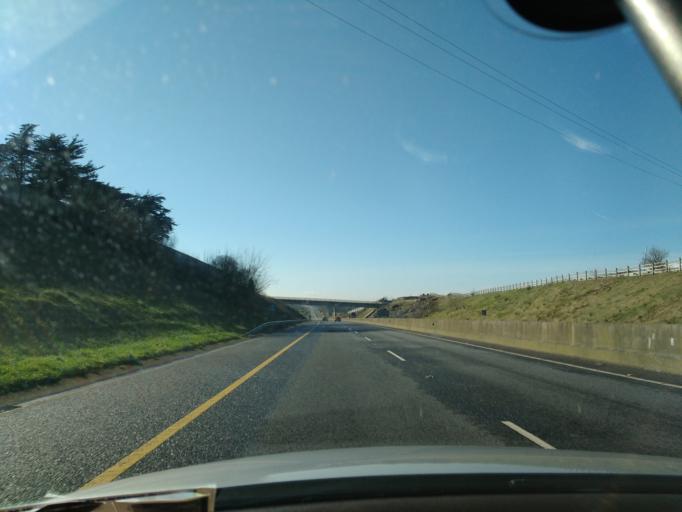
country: IE
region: Munster
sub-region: North Tipperary
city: Newport
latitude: 52.7472
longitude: -8.4312
